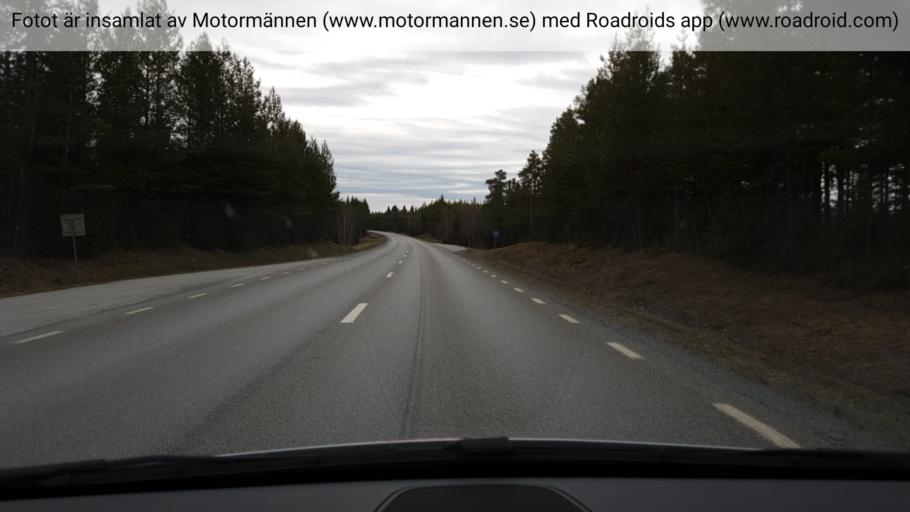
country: SE
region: Jaemtland
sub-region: Krokoms Kommun
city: Valla
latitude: 63.2932
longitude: 13.9267
